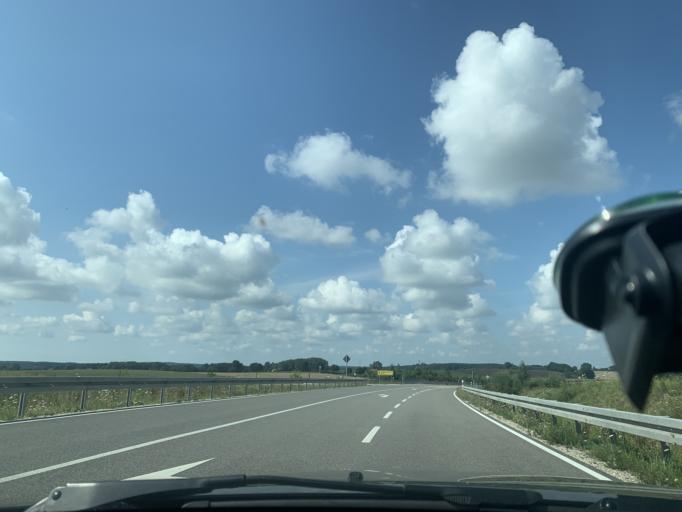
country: DE
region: Bavaria
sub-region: Upper Bavaria
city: Egenhofen
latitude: 48.2961
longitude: 11.1466
